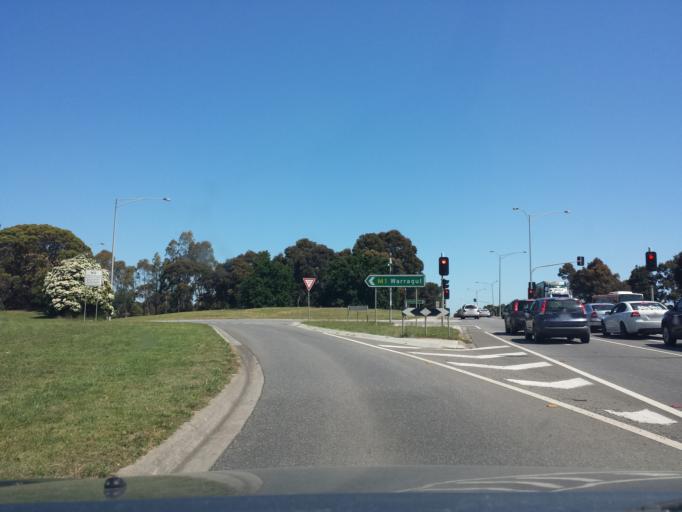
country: AU
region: Victoria
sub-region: Casey
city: Berwick
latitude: -38.0436
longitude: 145.3416
